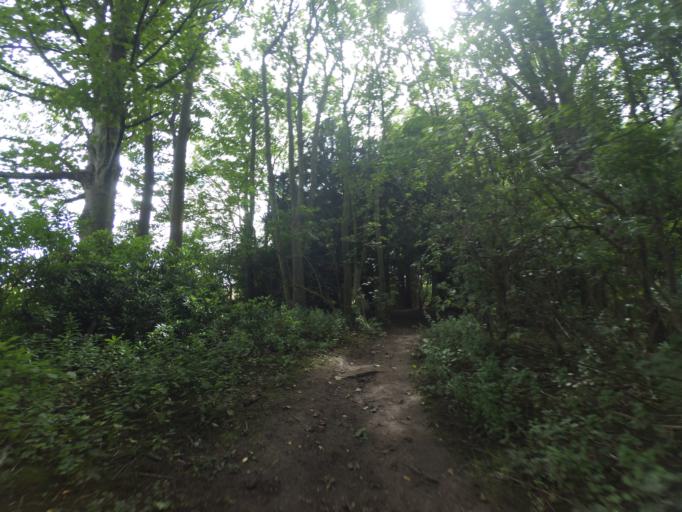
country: GB
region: Scotland
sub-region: Midlothian
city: Bonnyrigg
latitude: 55.9169
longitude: -3.1206
